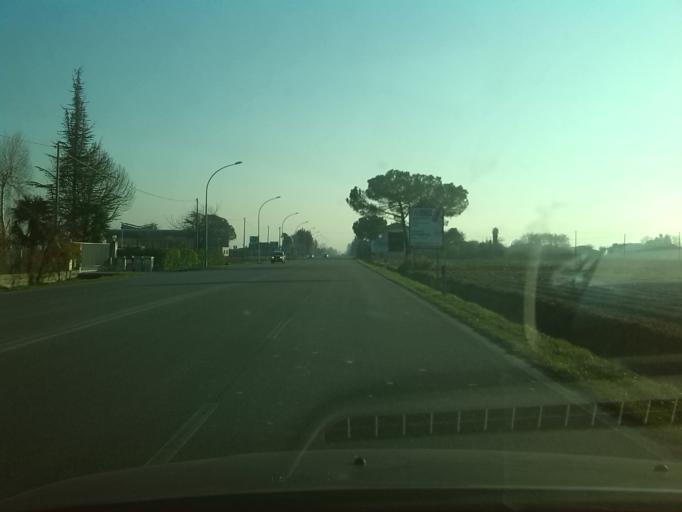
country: IT
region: Friuli Venezia Giulia
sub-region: Provincia di Udine
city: Pertegada
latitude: 45.7498
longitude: 13.0345
